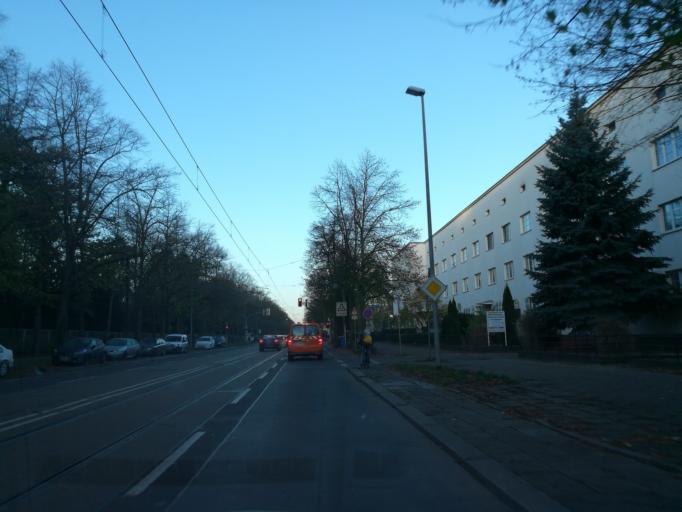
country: DE
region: Saxony-Anhalt
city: Diesdorf
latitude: 52.1288
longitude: 11.5838
